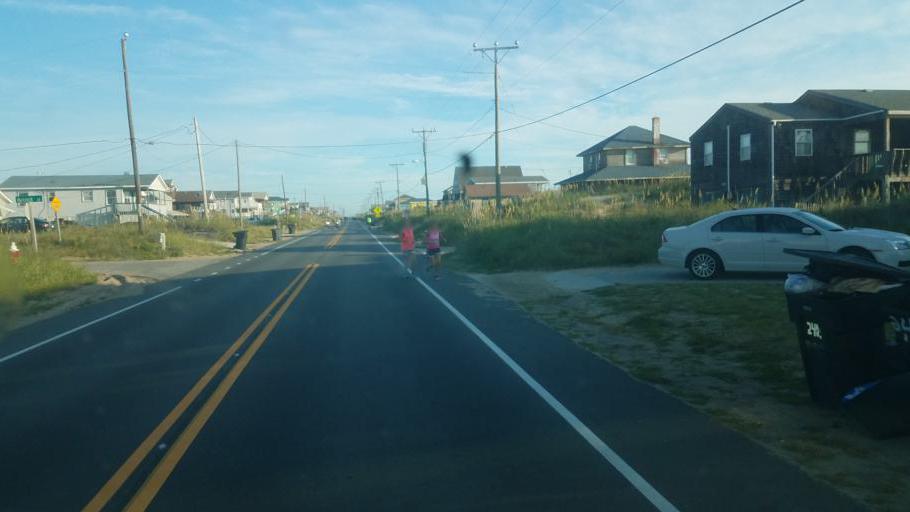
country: US
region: North Carolina
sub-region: Dare County
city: Kill Devil Hills
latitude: 36.0459
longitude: -75.6766
